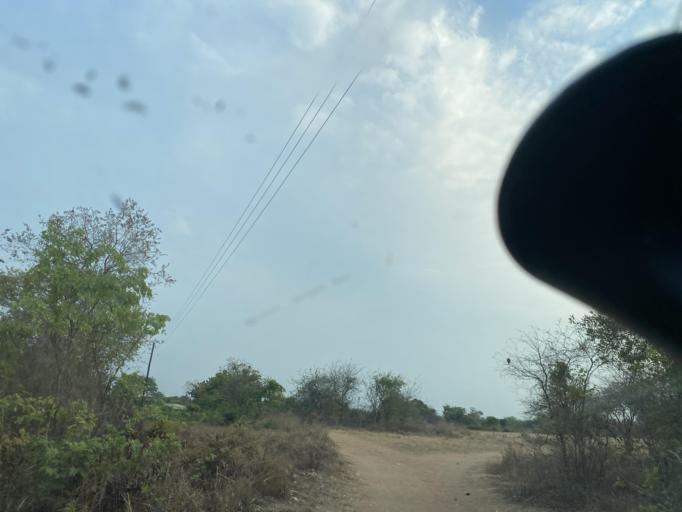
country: ZM
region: Lusaka
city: Chongwe
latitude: -15.2082
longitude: 28.5006
